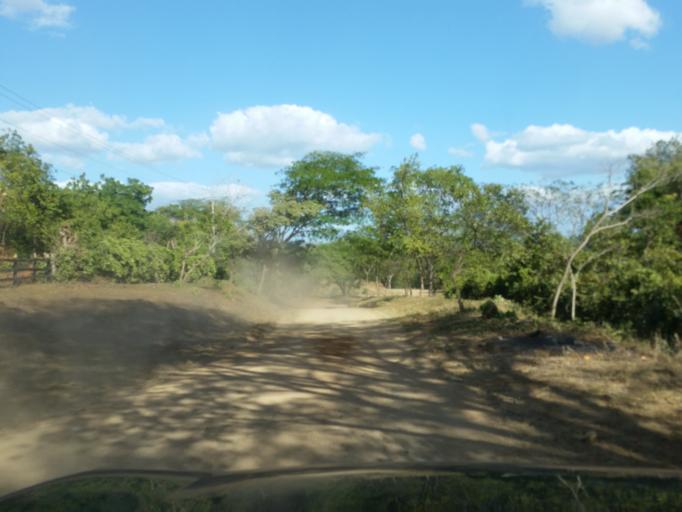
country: NI
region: Managua
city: Carlos Fonseca Amador
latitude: 11.9229
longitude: -86.5913
